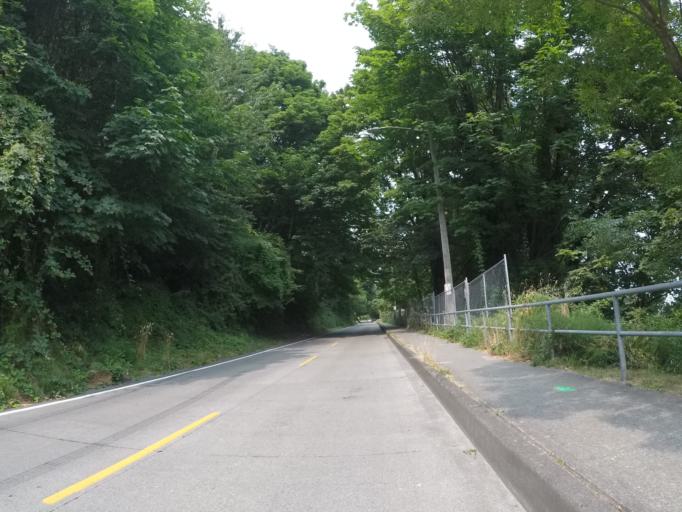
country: US
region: Washington
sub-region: King County
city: Seattle
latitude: 47.5910
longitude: -122.3829
